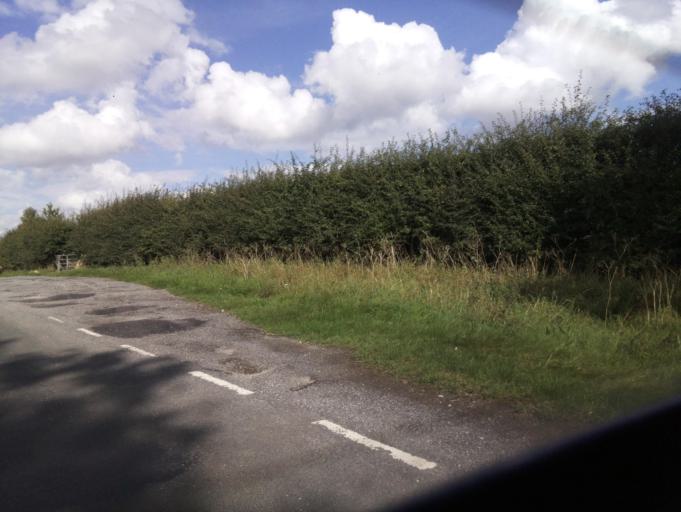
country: GB
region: England
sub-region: North Yorkshire
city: Leyburn
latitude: 54.3371
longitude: -1.8191
